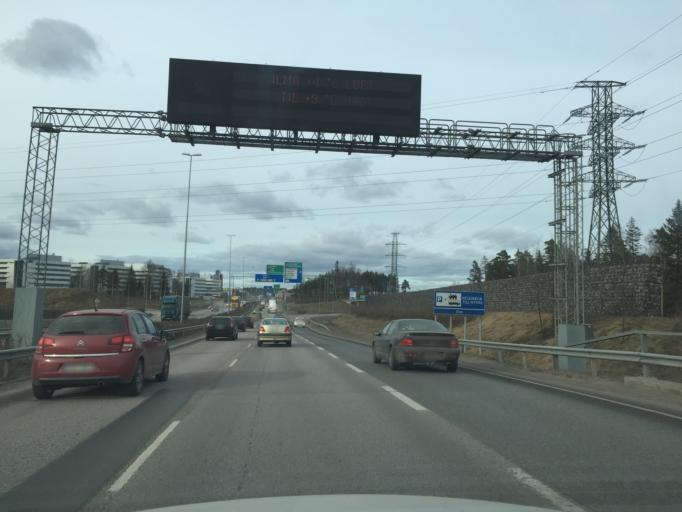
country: FI
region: Uusimaa
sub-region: Helsinki
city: Otaniemi
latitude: 60.2058
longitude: 24.8159
